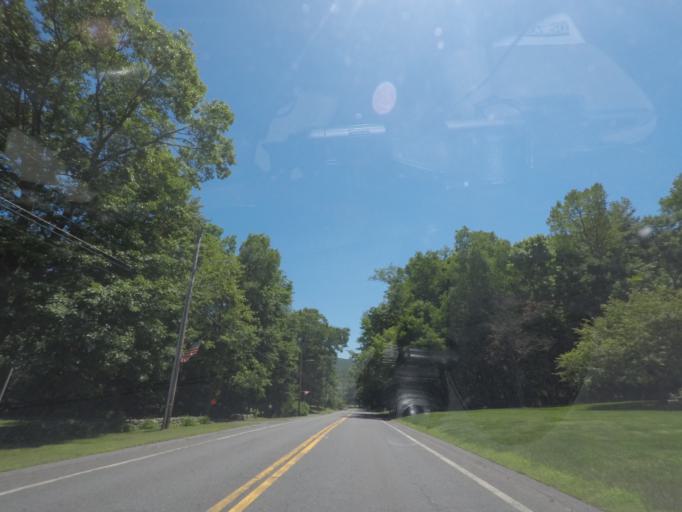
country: US
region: Massachusetts
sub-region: Berkshire County
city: Becket
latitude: 42.2705
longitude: -72.9679
